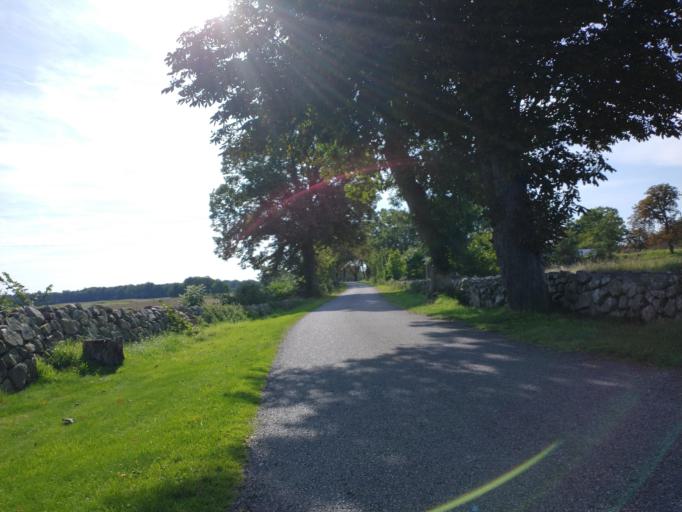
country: SE
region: Kalmar
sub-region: Kalmar Kommun
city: Lindsdal
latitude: 56.7785
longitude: 16.3227
